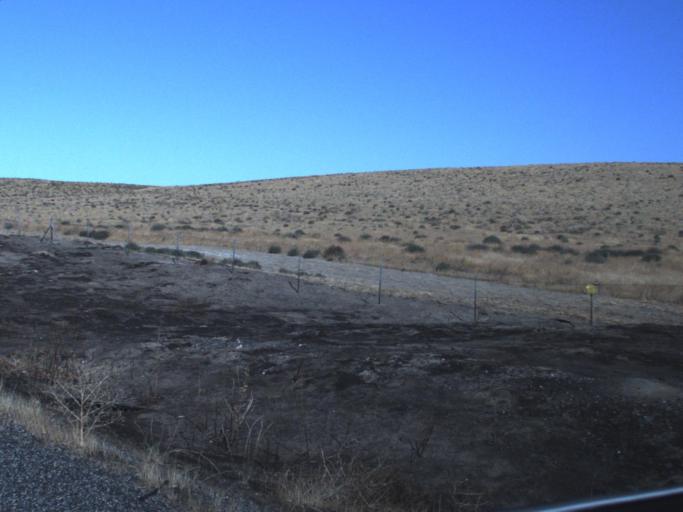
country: US
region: Washington
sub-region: Grant County
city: Desert Aire
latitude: 46.5621
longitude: -119.7118
